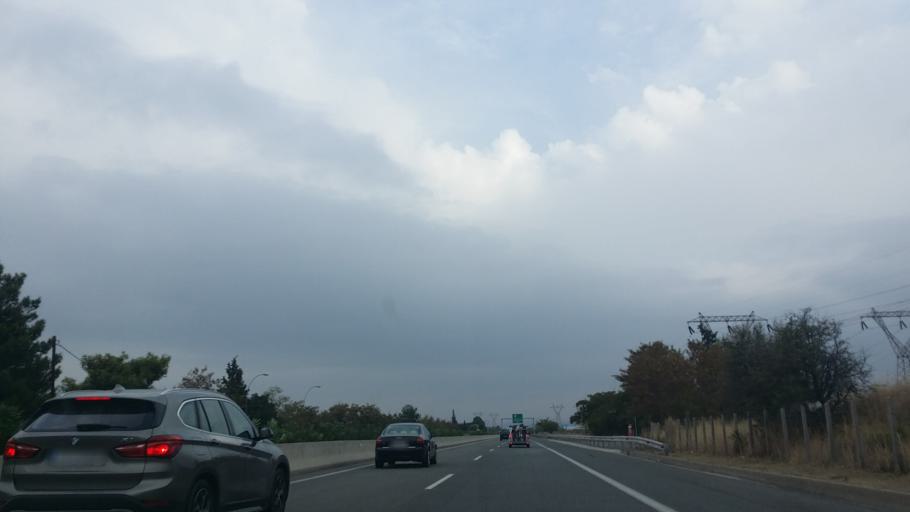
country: GR
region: Central Greece
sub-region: Nomos Voiotias
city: Schimatari
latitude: 38.3622
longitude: 23.5509
